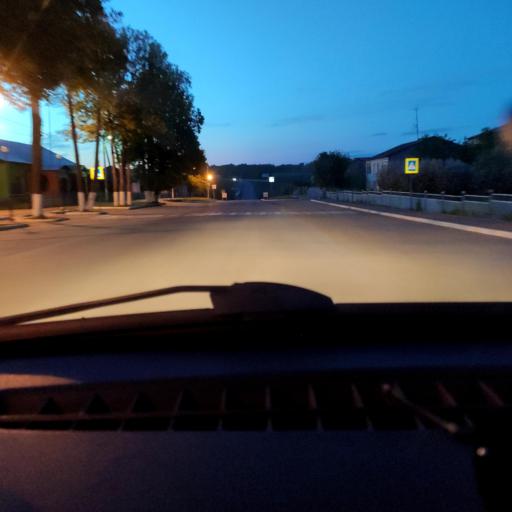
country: RU
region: Bashkortostan
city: Karmaskaly
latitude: 54.3716
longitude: 56.1720
